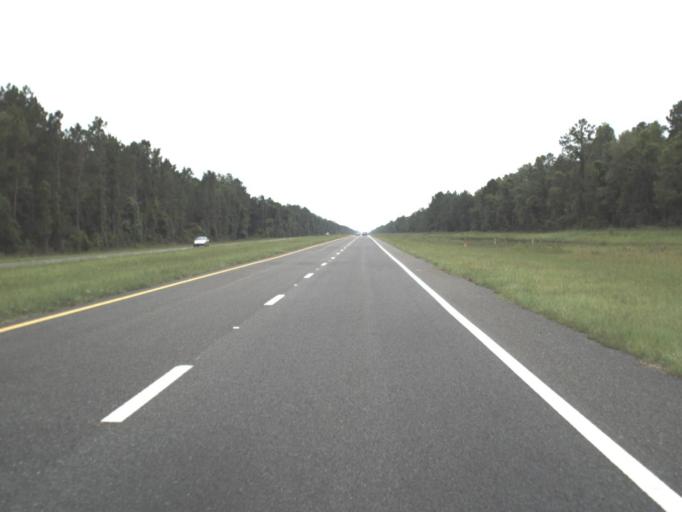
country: US
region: Florida
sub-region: Levy County
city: Chiefland
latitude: 29.3522
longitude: -82.7836
